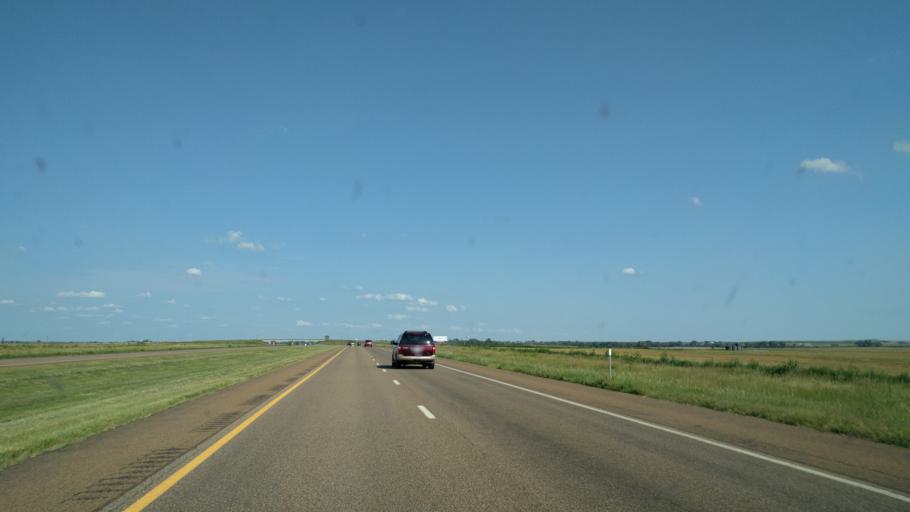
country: US
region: Kansas
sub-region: Ellis County
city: Ellis
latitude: 38.9526
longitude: -99.6038
